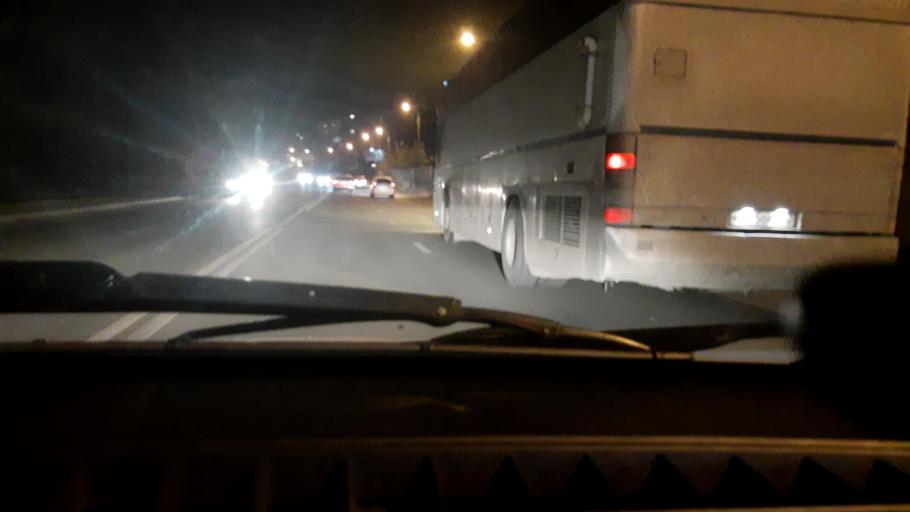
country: RU
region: Bashkortostan
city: Ufa
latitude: 54.8109
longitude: 56.0758
